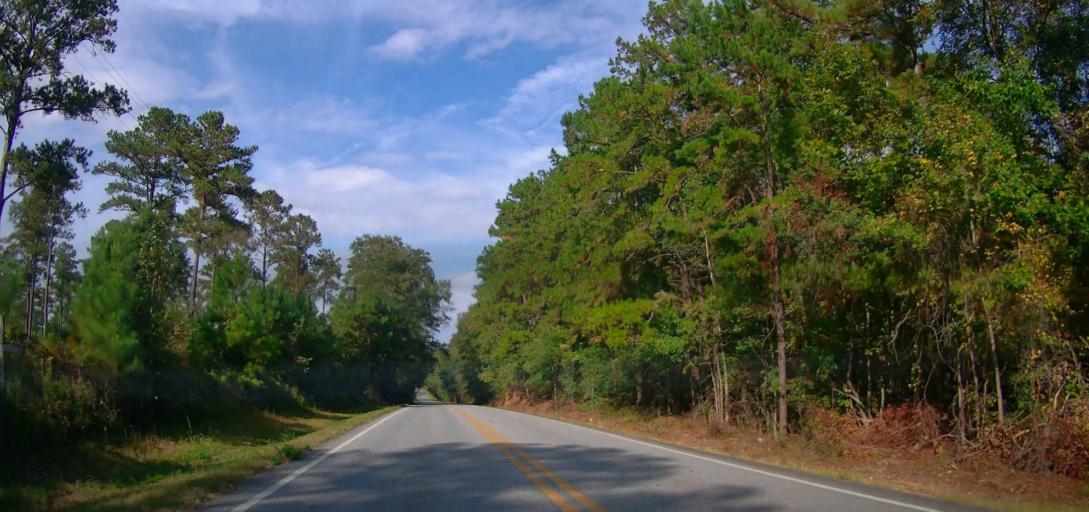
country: US
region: Georgia
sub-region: Thomas County
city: Thomasville
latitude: 30.9011
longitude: -84.0062
